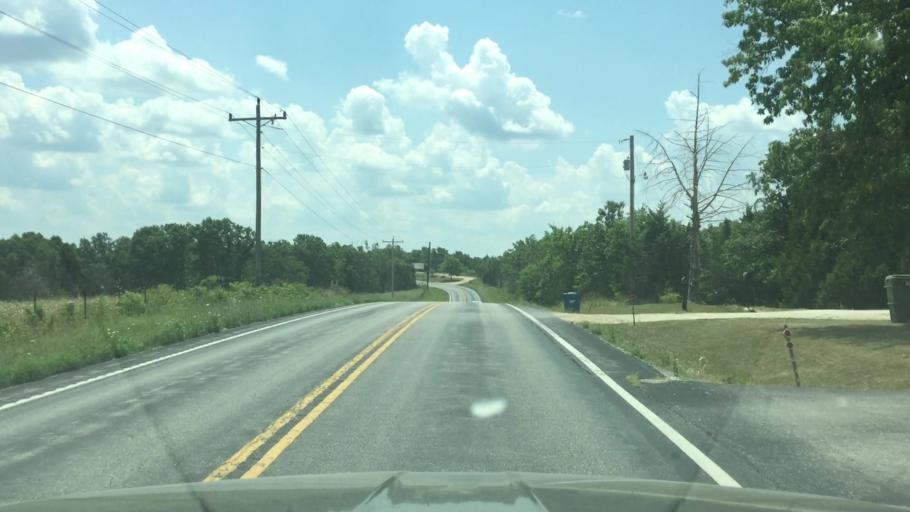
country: US
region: Missouri
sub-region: Miller County
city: Tuscumbia
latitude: 38.1087
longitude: -92.5023
